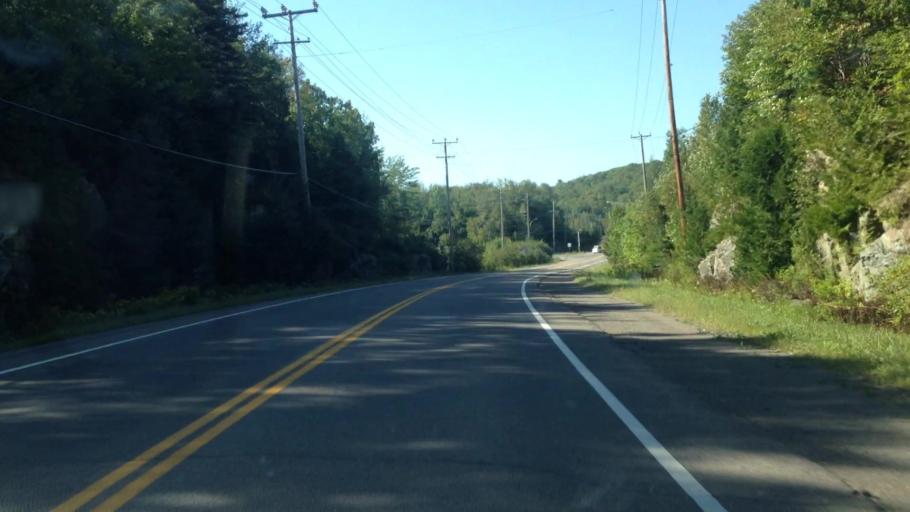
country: CA
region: Quebec
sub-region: Laurentides
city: Prevost
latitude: 45.9059
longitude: -74.0039
